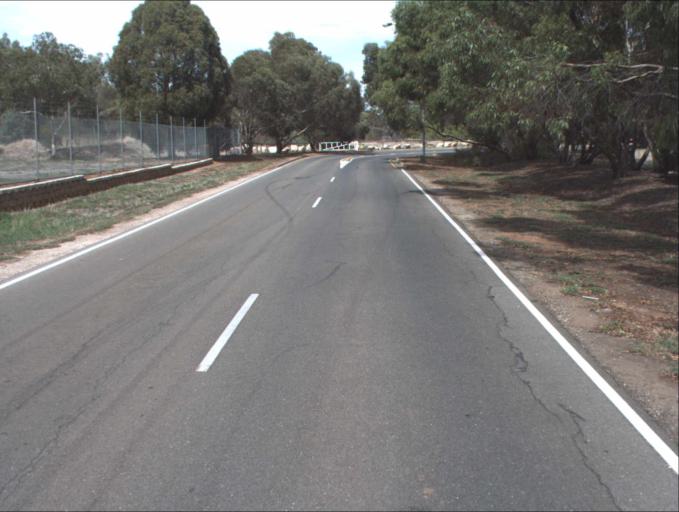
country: AU
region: South Australia
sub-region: Port Adelaide Enfield
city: Enfield
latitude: -34.8412
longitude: 138.6111
